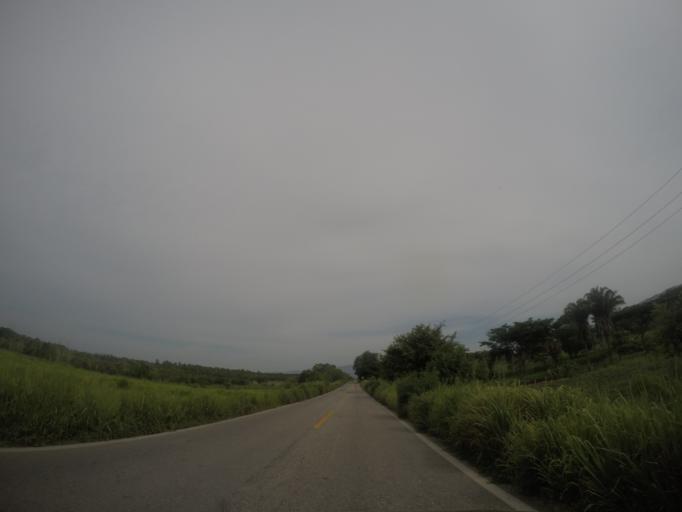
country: MX
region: Oaxaca
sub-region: Villa de Tututepec de Melchor Ocampo
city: Santa Rosa de Lima
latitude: 15.9774
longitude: -97.4046
